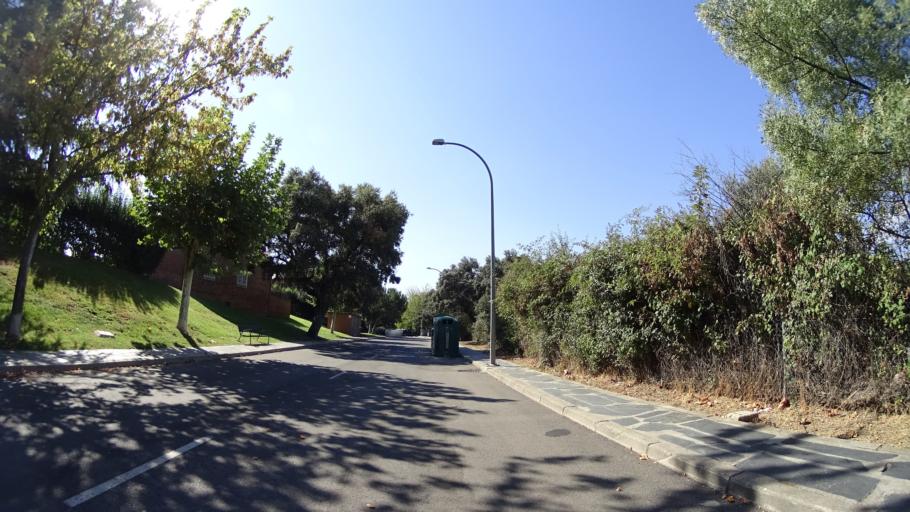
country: ES
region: Madrid
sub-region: Provincia de Madrid
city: Navalquejigo
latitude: 40.6089
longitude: -4.0325
